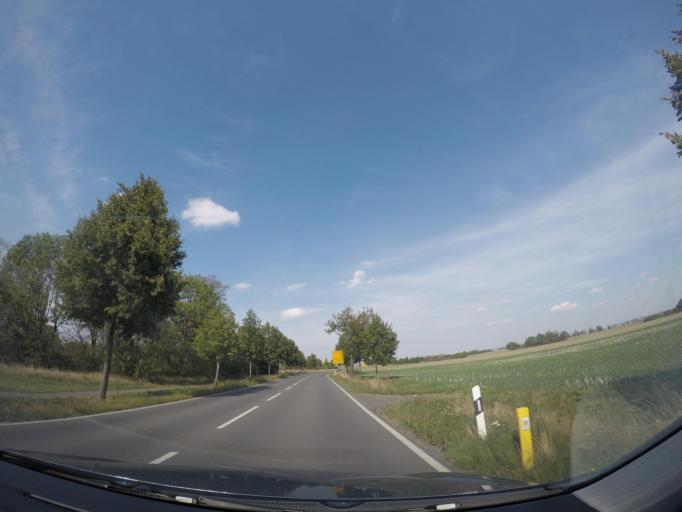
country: DE
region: Saxony-Anhalt
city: Wasserleben
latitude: 51.8967
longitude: 10.7669
